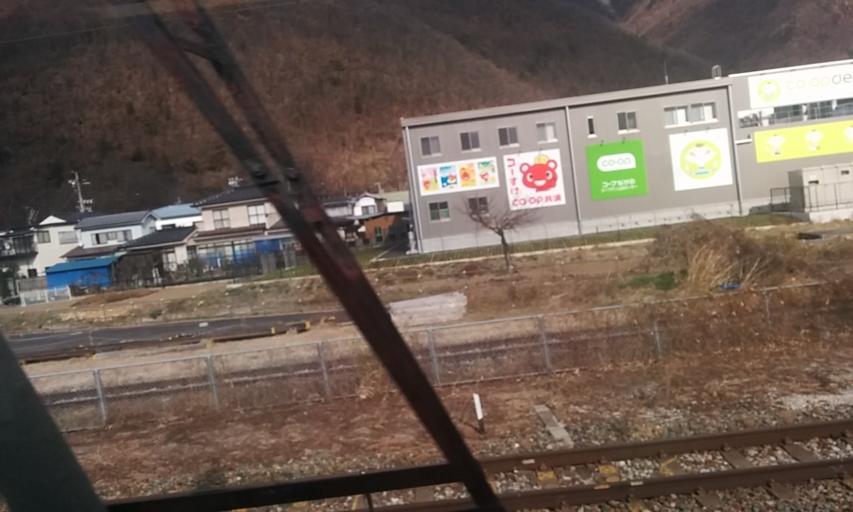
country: JP
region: Nagano
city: Ueda
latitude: 36.4164
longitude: 138.2105
